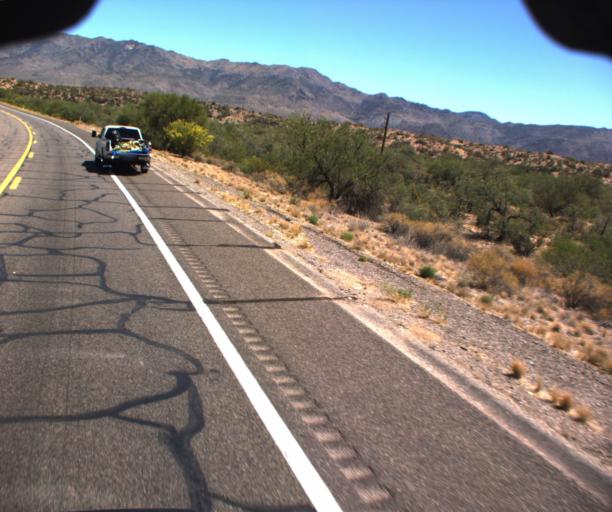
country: US
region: Arizona
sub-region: Yavapai County
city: Congress
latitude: 34.1687
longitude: -112.8346
